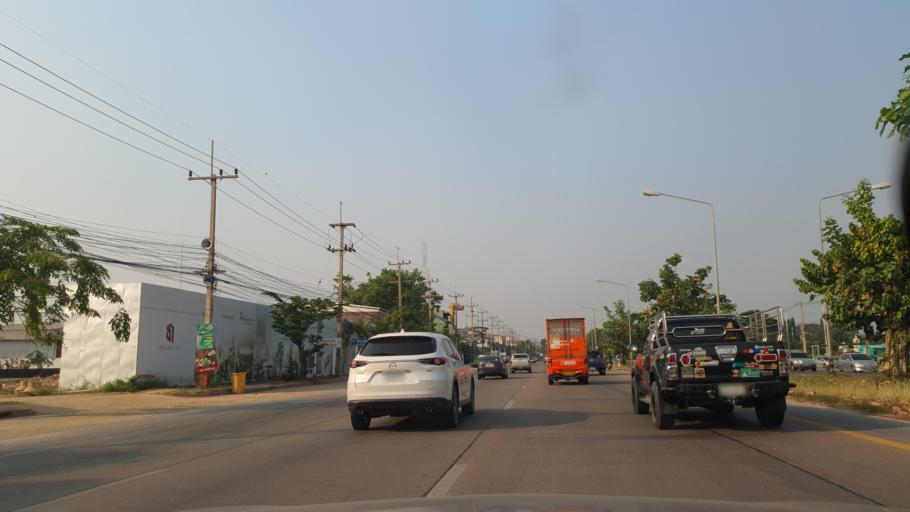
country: TH
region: Phitsanulok
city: Phitsanulok
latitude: 16.7990
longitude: 100.2136
